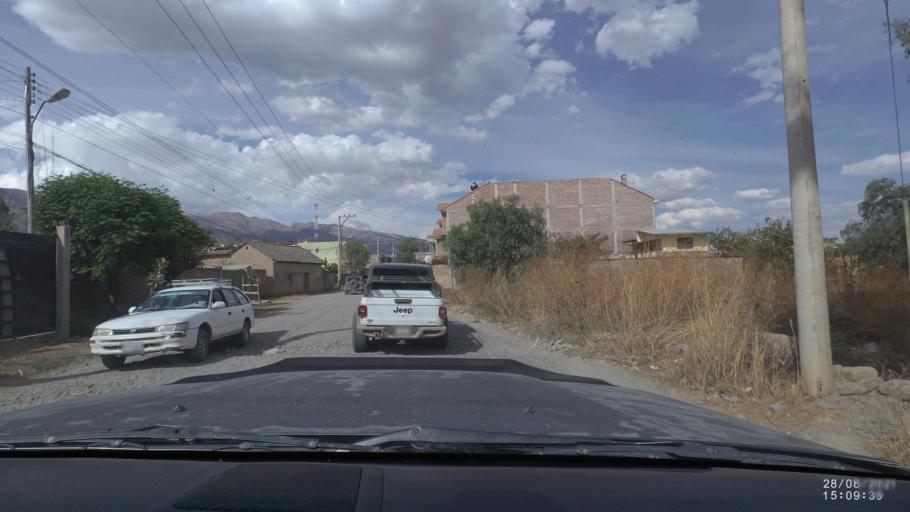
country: BO
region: Cochabamba
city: Cochabamba
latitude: -17.3386
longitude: -66.2698
